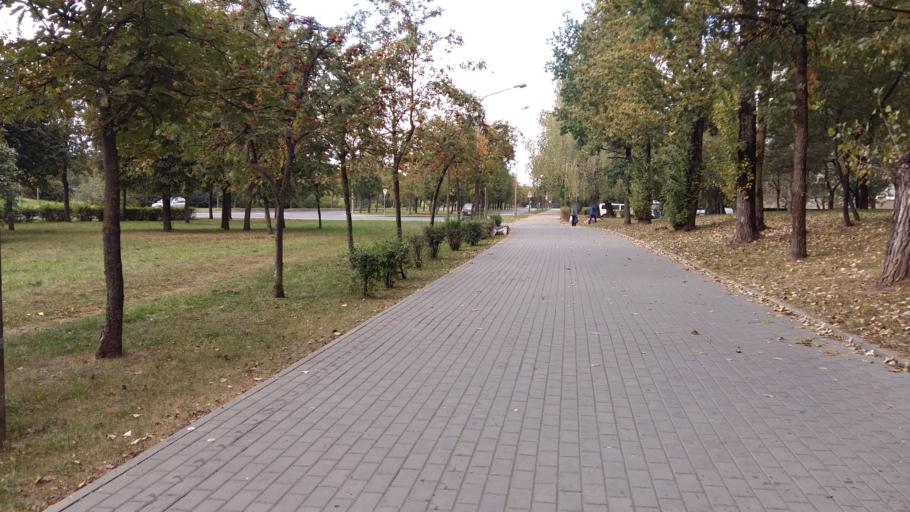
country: BY
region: Grodnenskaya
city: Hrodna
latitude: 53.6996
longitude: 23.7995
